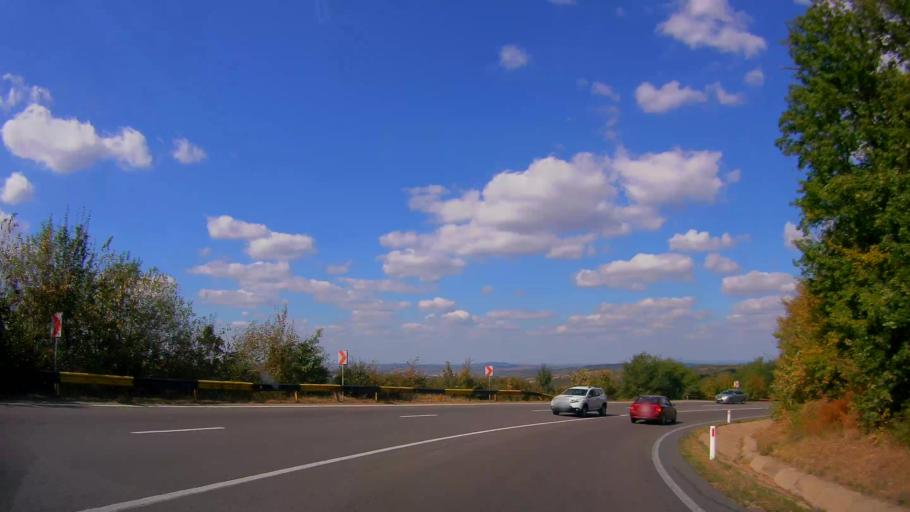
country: RO
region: Salaj
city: Zalau
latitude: 47.1564
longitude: 23.0886
